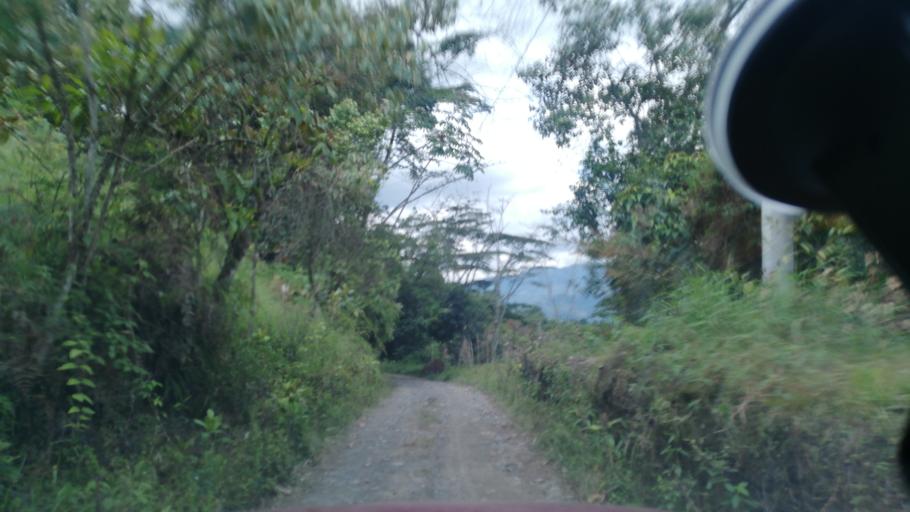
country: CO
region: Cundinamarca
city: Vergara
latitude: 5.2076
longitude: -74.2867
